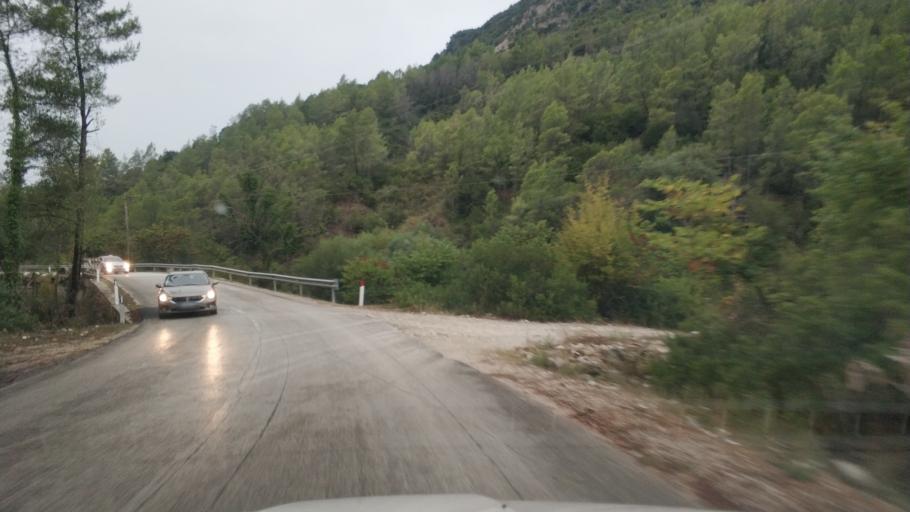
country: AL
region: Vlore
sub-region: Rrethi i Delvines
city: Mesopotam
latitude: 39.9213
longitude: 20.1523
